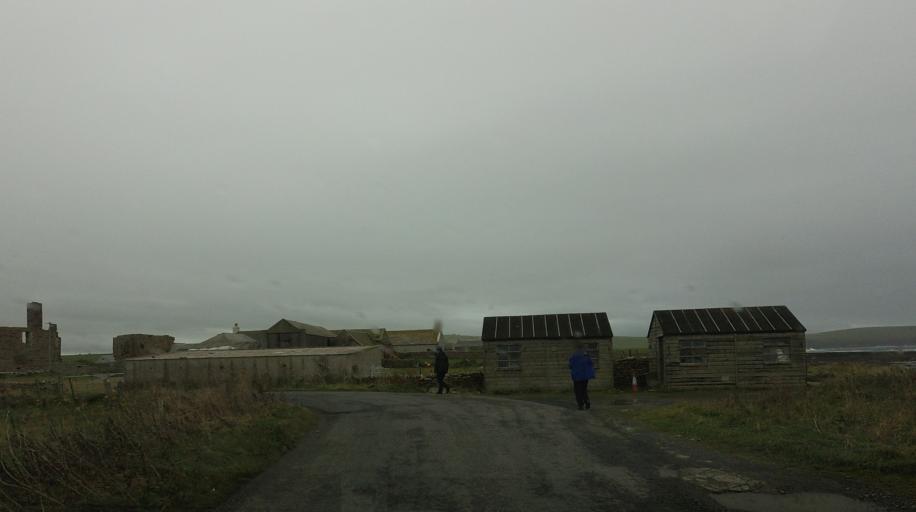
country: GB
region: Scotland
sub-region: Orkney Islands
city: Stromness
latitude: 59.1305
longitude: -3.3166
